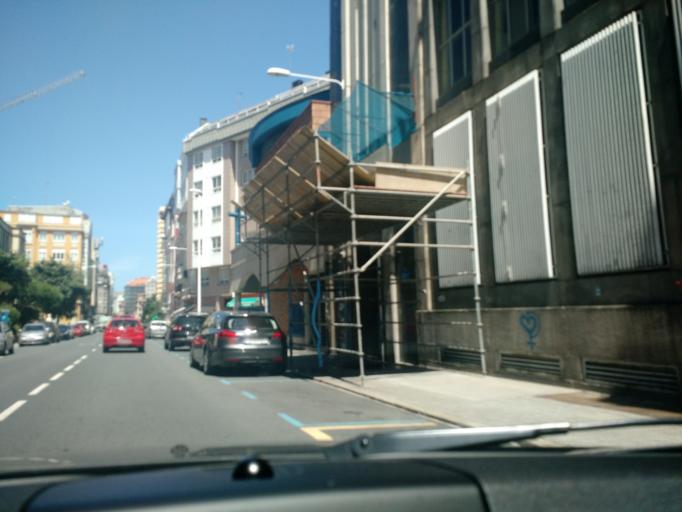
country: ES
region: Galicia
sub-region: Provincia da Coruna
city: A Coruna
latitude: 43.3548
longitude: -8.4050
